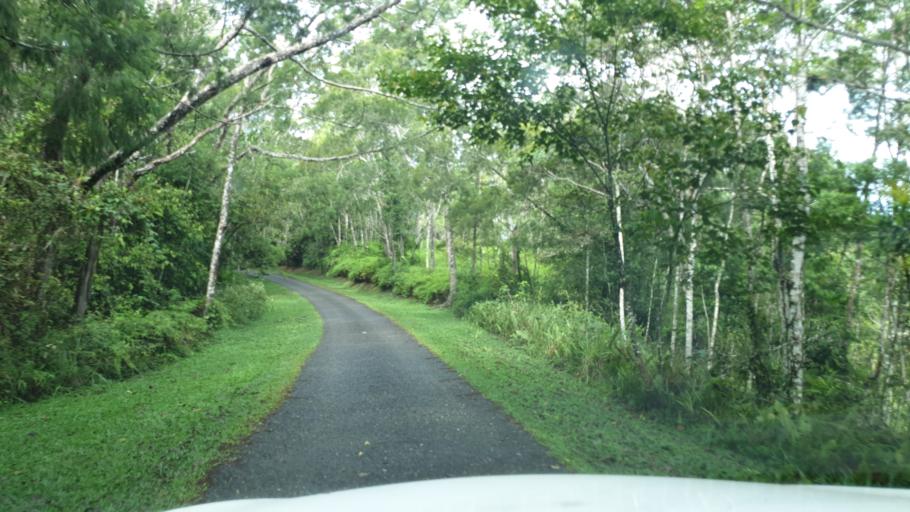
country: PG
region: National Capital
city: Port Moresby
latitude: -9.4335
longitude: 147.3681
